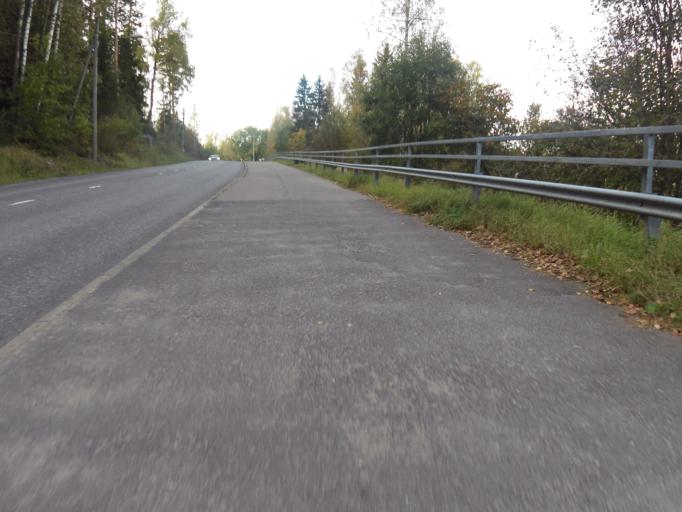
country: FI
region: Uusimaa
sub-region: Helsinki
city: Kilo
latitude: 60.2721
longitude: 24.7519
